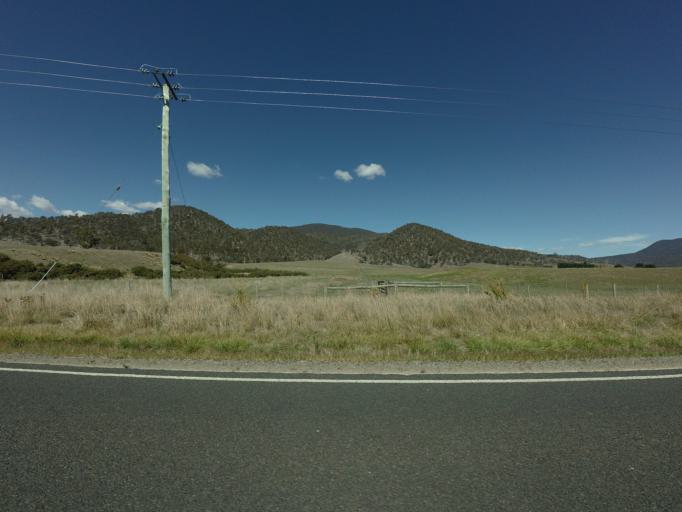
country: AU
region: Tasmania
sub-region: Break O'Day
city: St Helens
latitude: -41.6999
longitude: 147.8573
